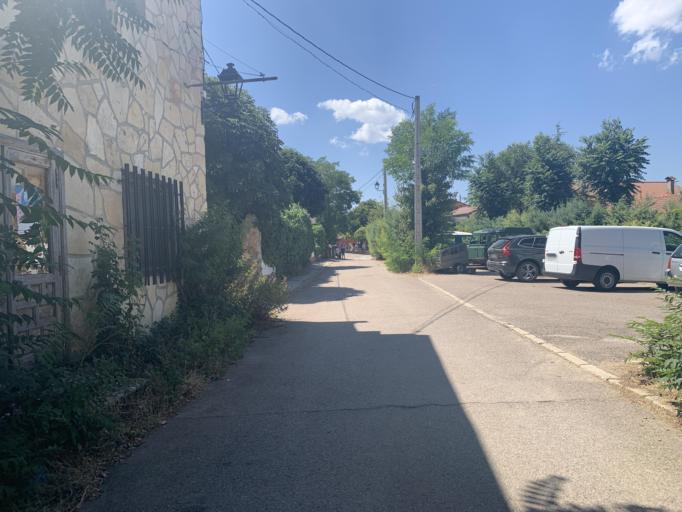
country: ES
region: Castille-La Mancha
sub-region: Provincia de Guadalajara
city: Zaorejas
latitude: 40.7622
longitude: -2.1993
